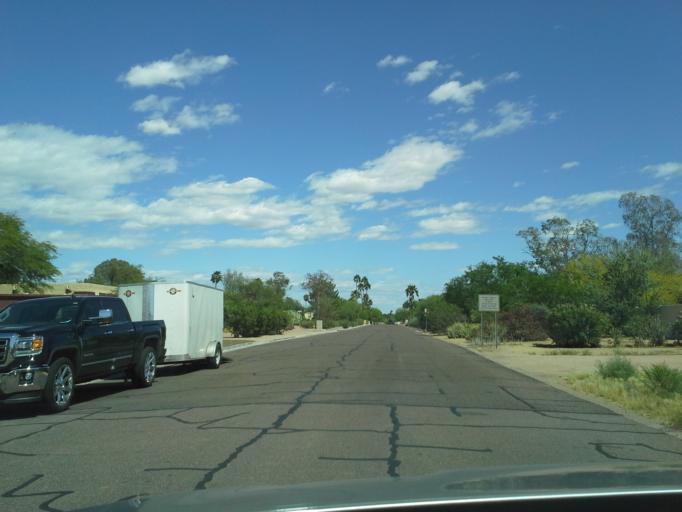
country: US
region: Arizona
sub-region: Maricopa County
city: Paradise Valley
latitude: 33.5750
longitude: -111.9502
